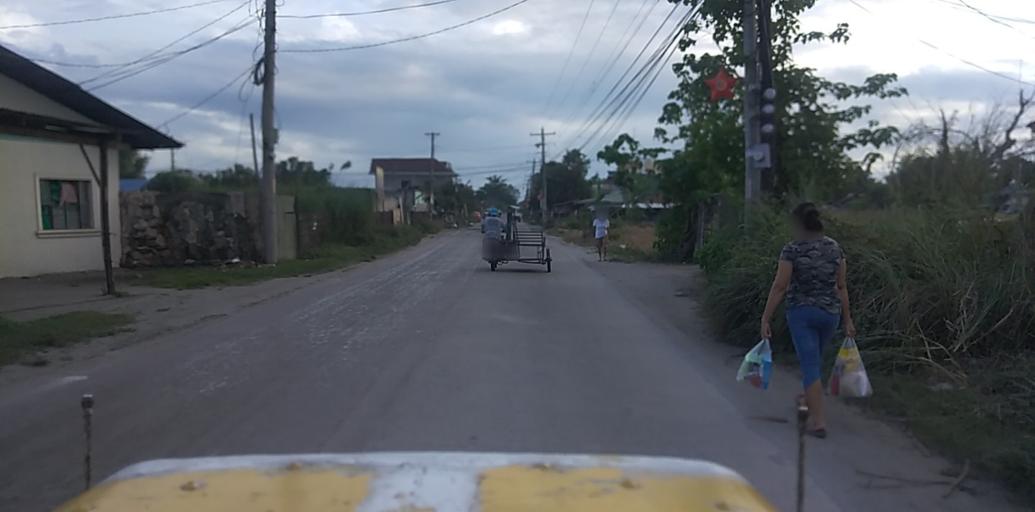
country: PH
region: Central Luzon
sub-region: Province of Pampanga
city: San Antonio
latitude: 15.1588
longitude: 120.6861
